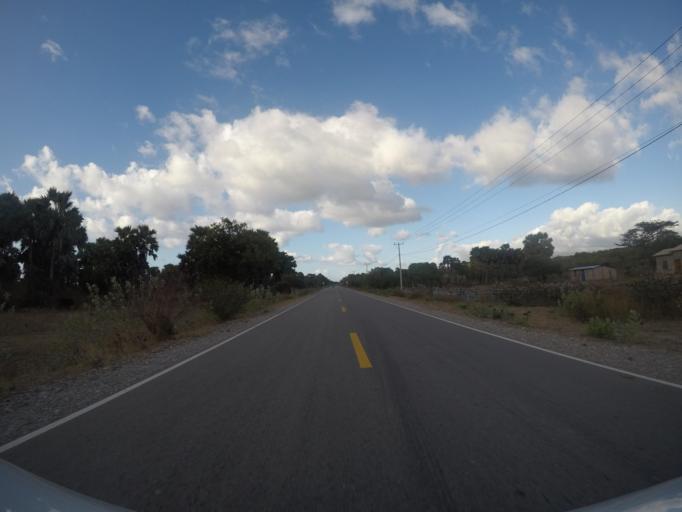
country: TL
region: Lautem
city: Lospalos
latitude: -8.3857
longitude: 126.8561
